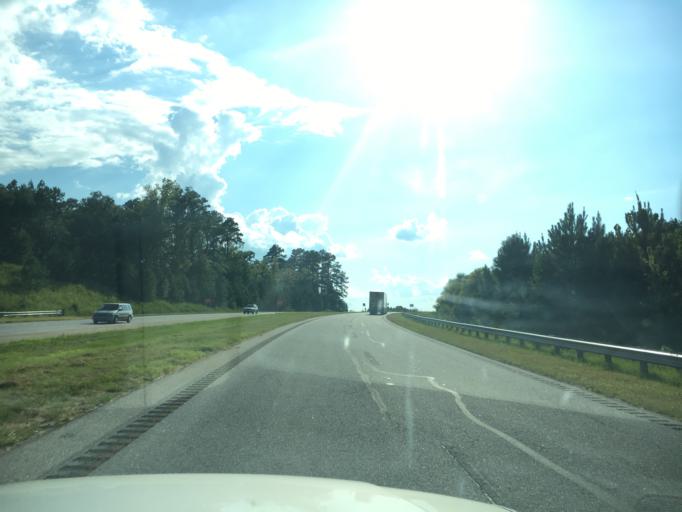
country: US
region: South Carolina
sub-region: Greenwood County
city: Ninety Six
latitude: 34.2907
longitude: -82.0188
